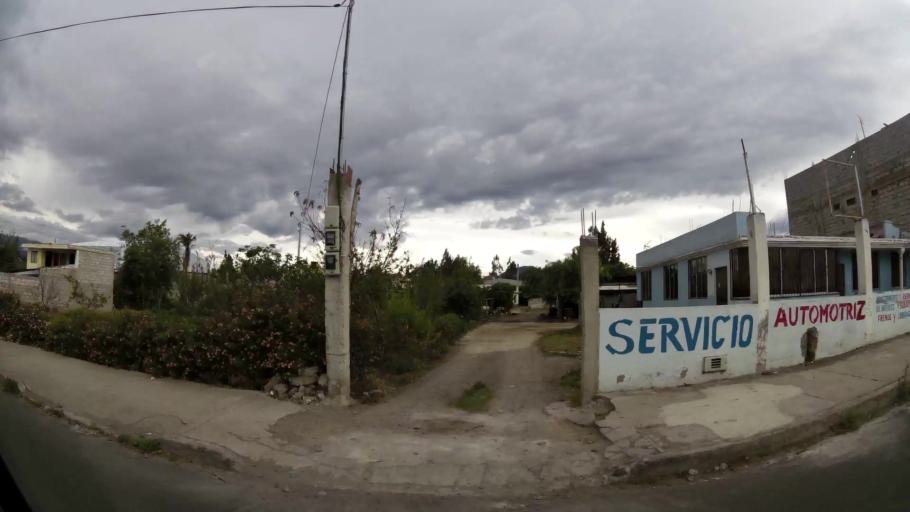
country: EC
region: Tungurahua
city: Ambato
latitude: -1.2802
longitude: -78.6211
